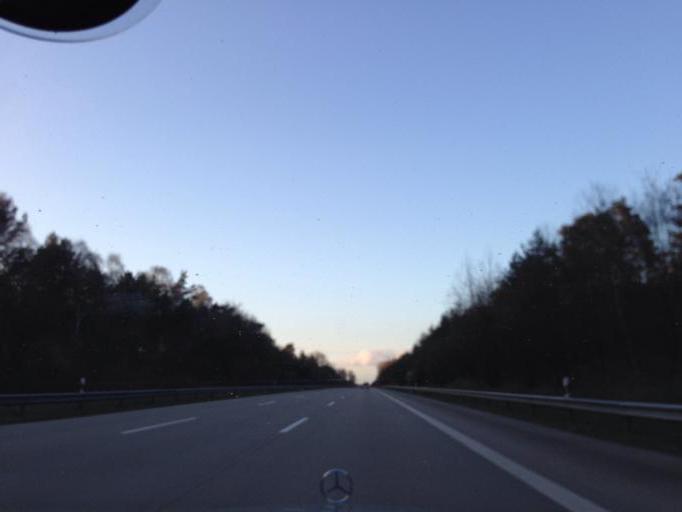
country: DE
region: Lower Saxony
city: Bispingen
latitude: 53.0468
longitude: 9.9525
